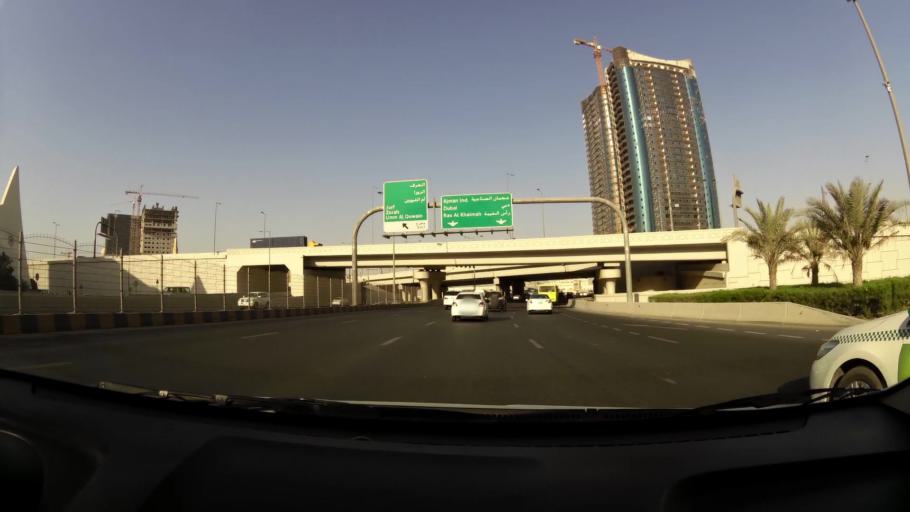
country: AE
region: Ajman
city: Ajman
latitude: 25.3913
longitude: 55.4708
